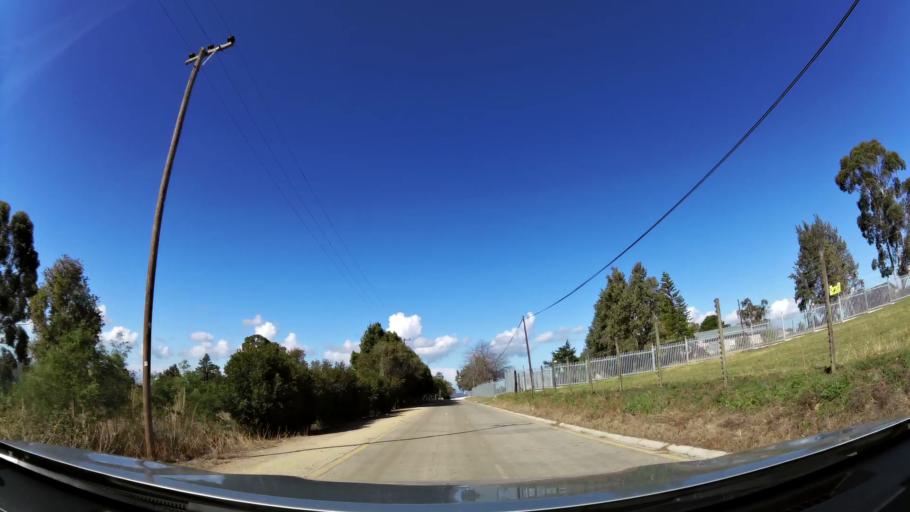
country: ZA
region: Western Cape
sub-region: Eden District Municipality
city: George
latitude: -33.9388
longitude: 22.4052
